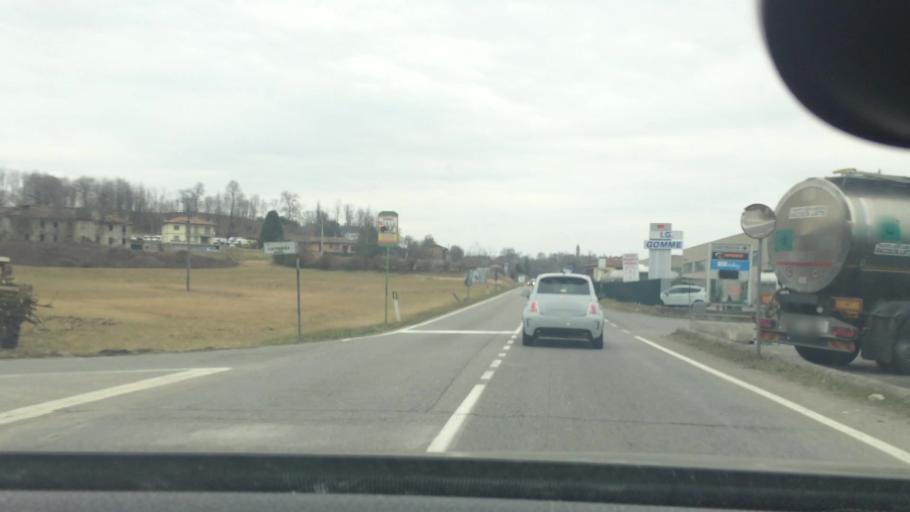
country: IT
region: Lombardy
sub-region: Provincia di Como
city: Nobile-Monguzzo
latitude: 45.7684
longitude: 9.2295
